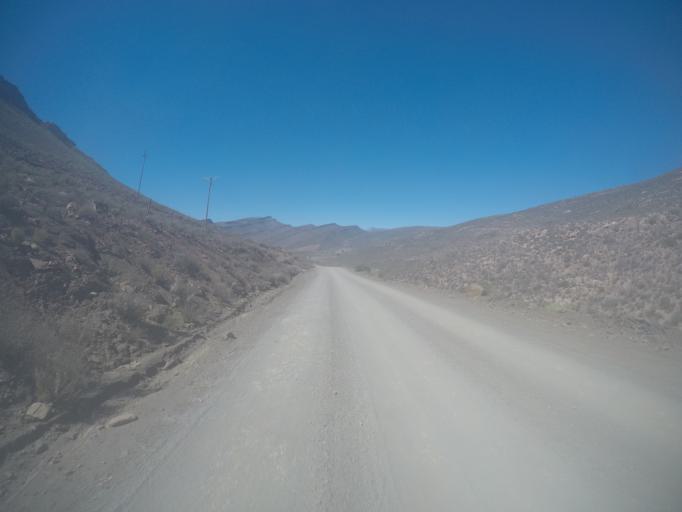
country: ZA
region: Western Cape
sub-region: West Coast District Municipality
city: Clanwilliam
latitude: -32.5400
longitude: 19.3565
